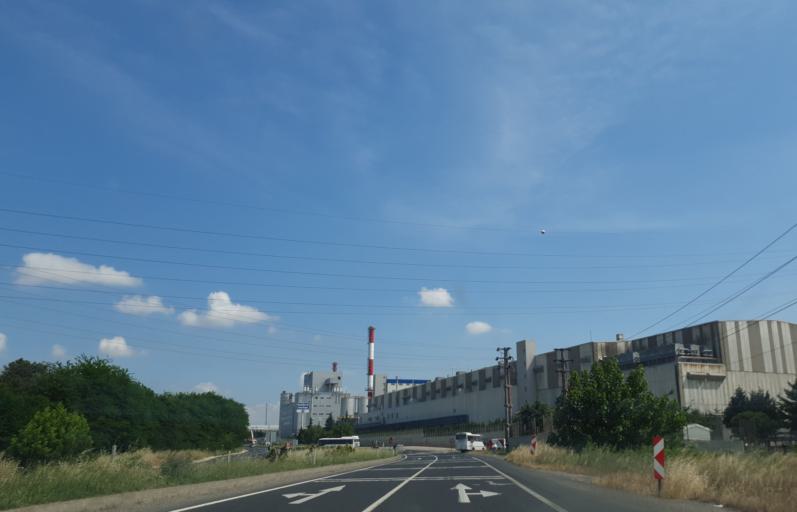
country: TR
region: Tekirdag
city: Marmaracik
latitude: 41.2427
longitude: 27.6942
